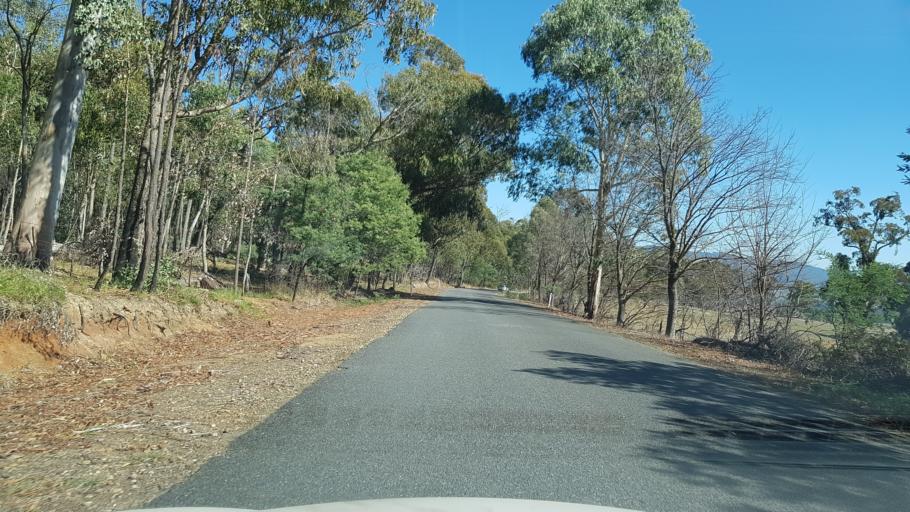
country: AU
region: Victoria
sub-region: Mansfield
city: Mansfield
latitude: -36.8164
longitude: 146.4659
